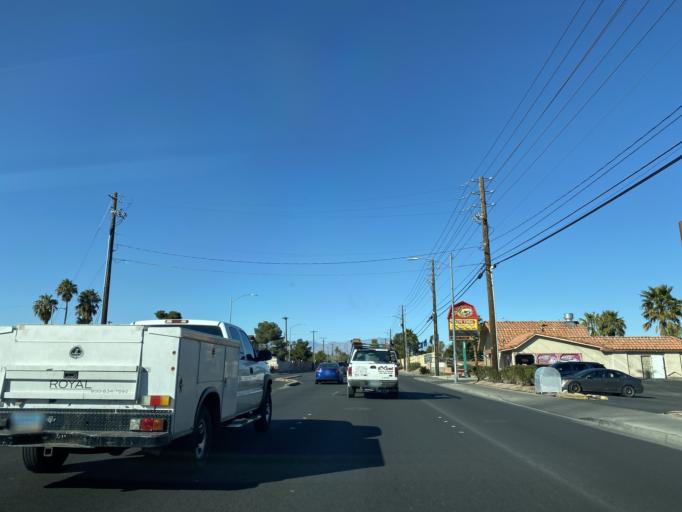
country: US
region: Nevada
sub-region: Clark County
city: Las Vegas
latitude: 36.1457
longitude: -115.1908
